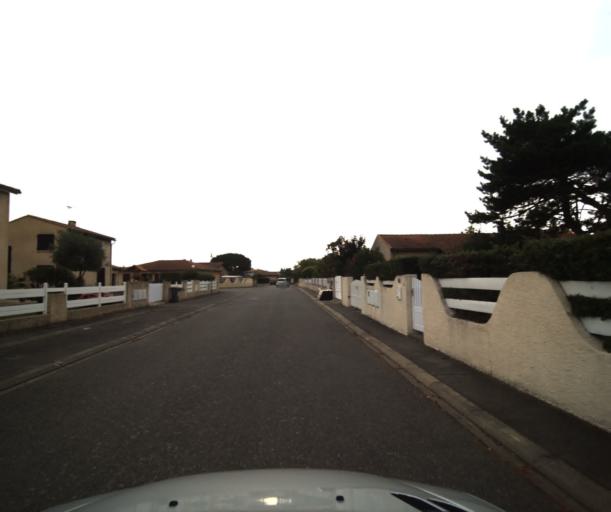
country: FR
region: Midi-Pyrenees
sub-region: Departement de la Haute-Garonne
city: Pinsaguel
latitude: 43.5159
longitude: 1.3912
